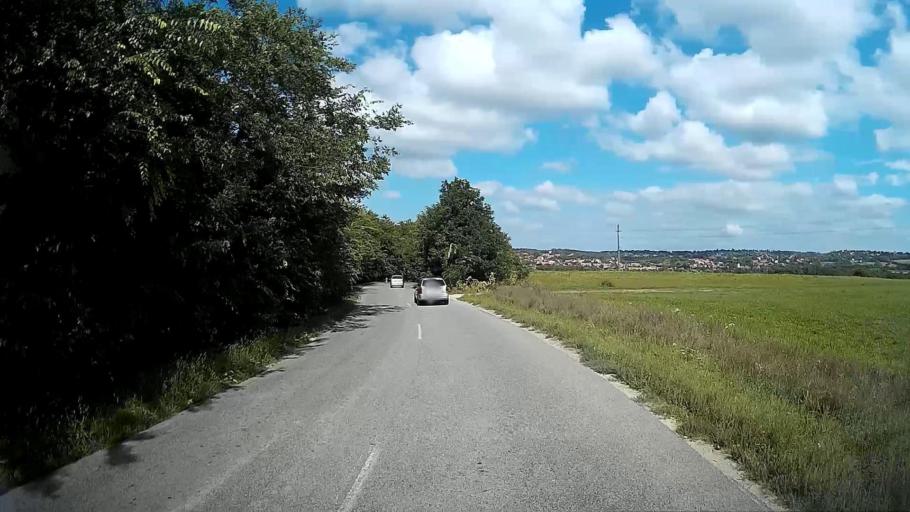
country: HU
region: Pest
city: Mogyorod
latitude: 47.5870
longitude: 19.2318
